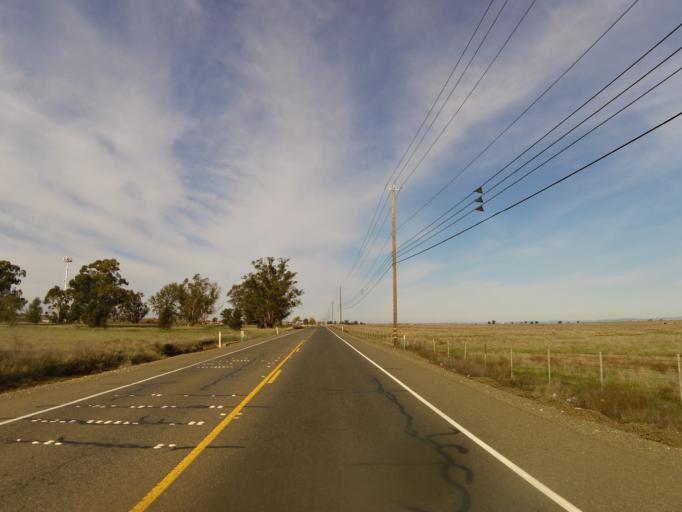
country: US
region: California
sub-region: Sacramento County
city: Wilton
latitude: 38.4870
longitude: -121.2422
